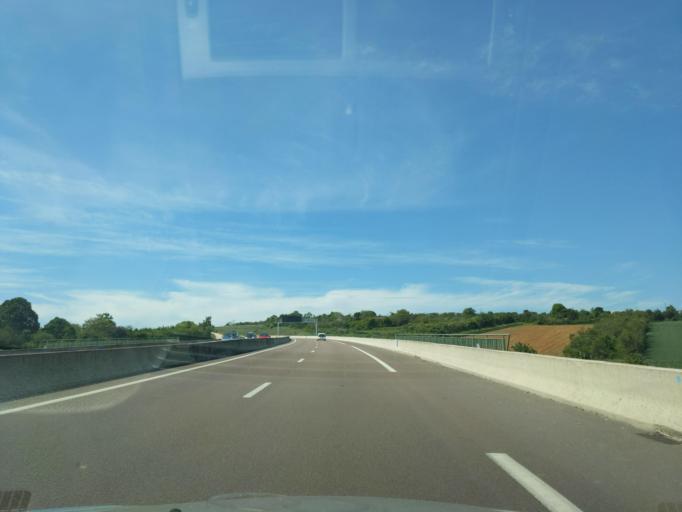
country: FR
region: Bourgogne
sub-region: Departement de la Cote-d'Or
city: Ahuy
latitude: 47.3580
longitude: 5.0226
